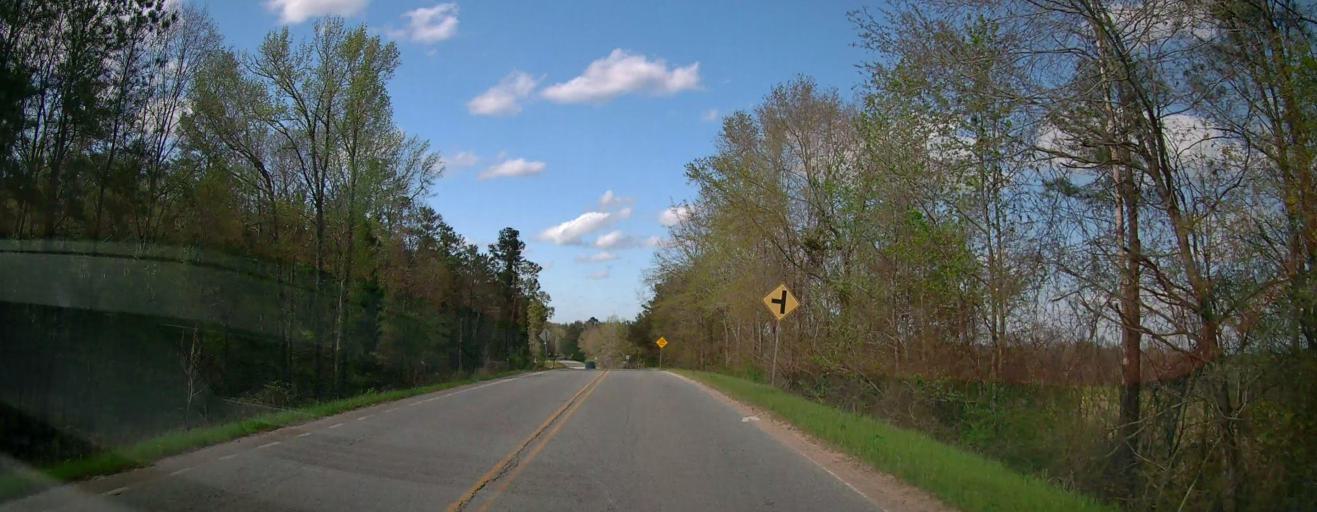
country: US
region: Georgia
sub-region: Wilkinson County
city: Gordon
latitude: 32.9564
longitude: -83.2899
